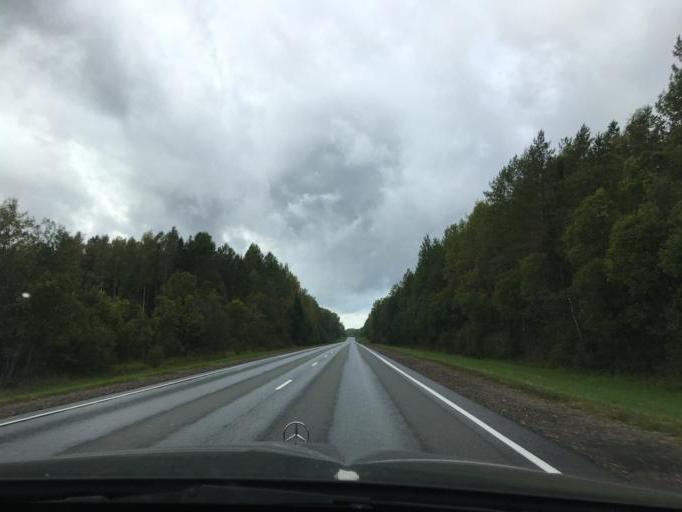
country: RU
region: Tverskaya
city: Nelidovo
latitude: 56.2663
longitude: 32.8889
